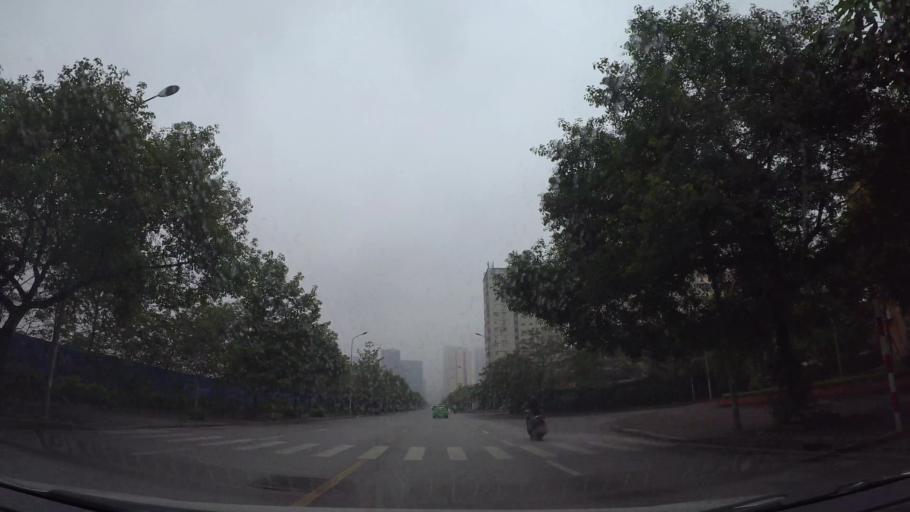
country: VN
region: Ha Noi
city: Cau Giay
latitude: 21.0146
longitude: 105.7902
